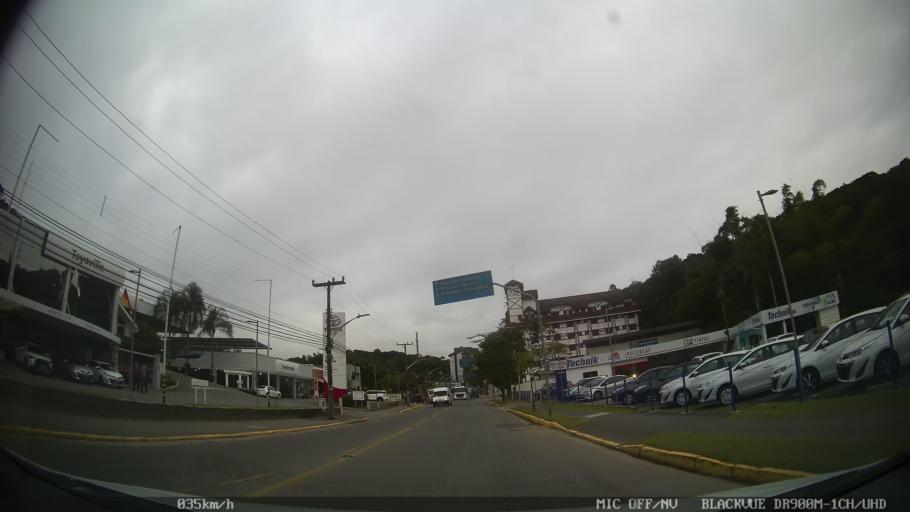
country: BR
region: Santa Catarina
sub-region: Joinville
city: Joinville
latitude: -26.2955
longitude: -48.8810
